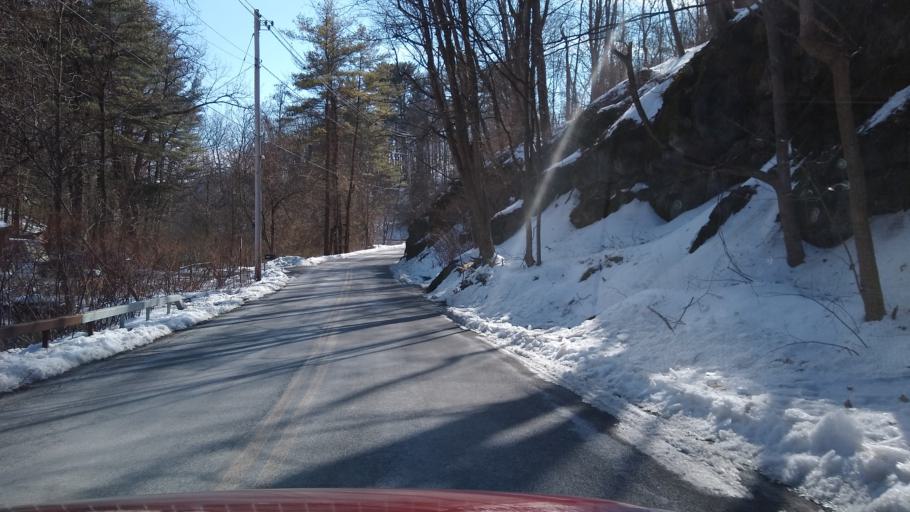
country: US
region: New York
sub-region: Ulster County
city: Kingston
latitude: 41.9170
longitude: -74.0121
